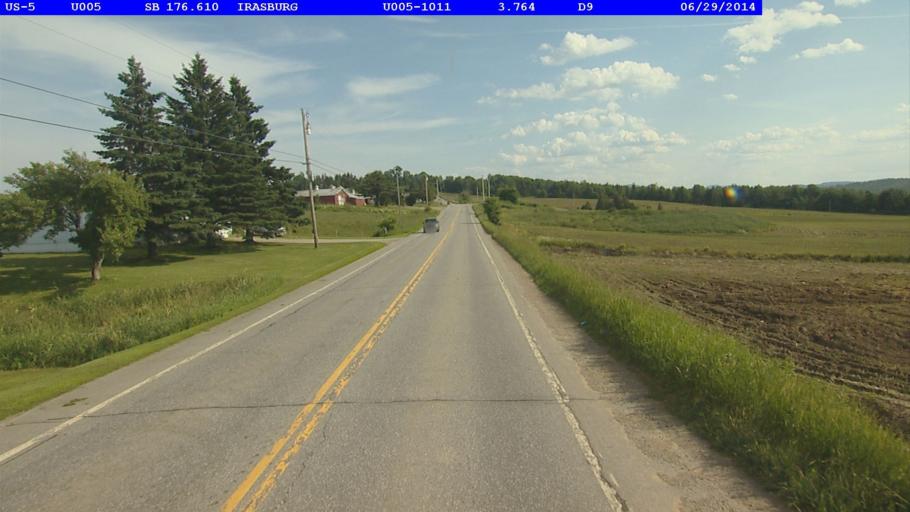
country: US
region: Vermont
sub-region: Orleans County
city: Newport
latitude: 44.8461
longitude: -72.2621
